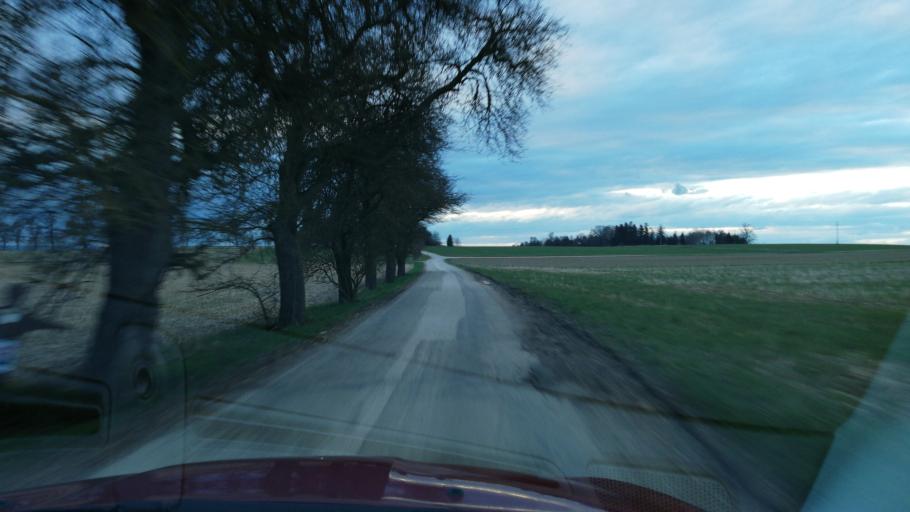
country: AT
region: Upper Austria
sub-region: Wels-Land
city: Buchkirchen
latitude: 48.2108
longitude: 14.0186
